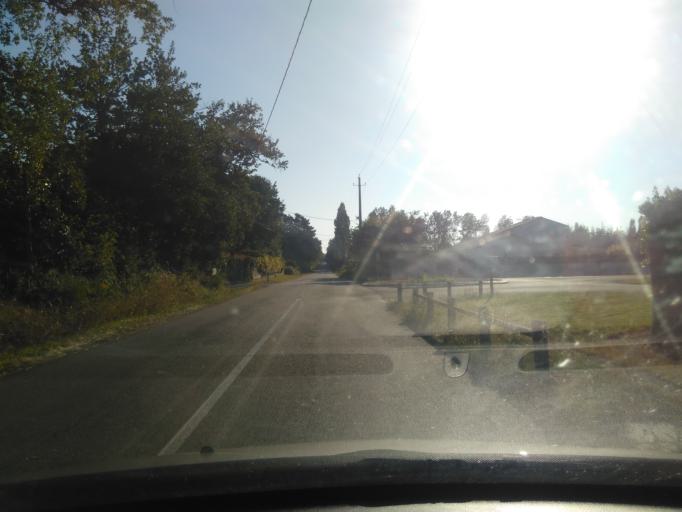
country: FR
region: Pays de la Loire
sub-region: Departement de la Vendee
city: Mouilleron-le-Captif
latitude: 46.7329
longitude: -1.4259
